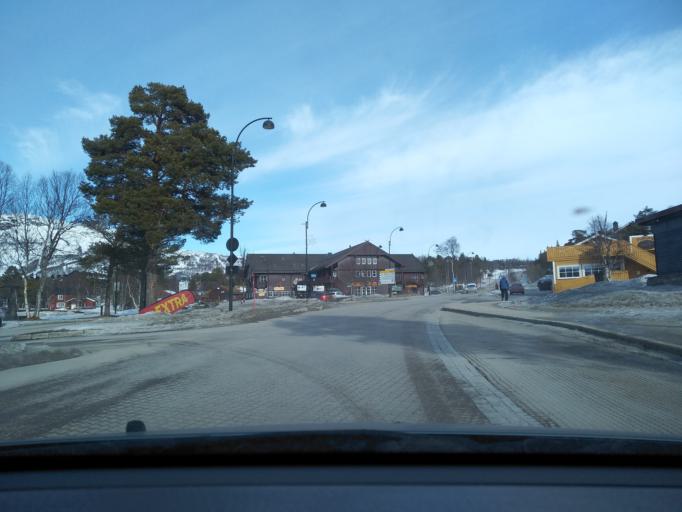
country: NO
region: Aust-Agder
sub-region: Bykle
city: Hovden
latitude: 59.5596
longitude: 7.3567
